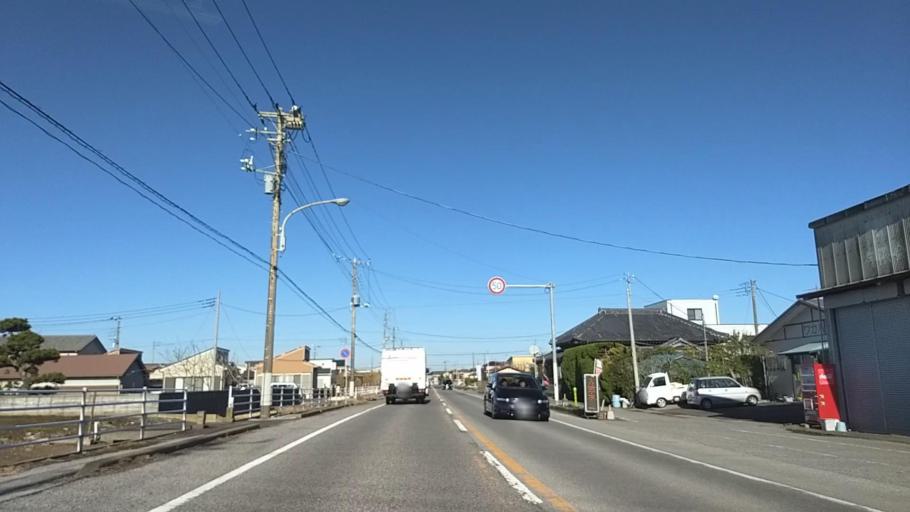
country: JP
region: Chiba
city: Togane
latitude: 35.5213
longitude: 140.4429
